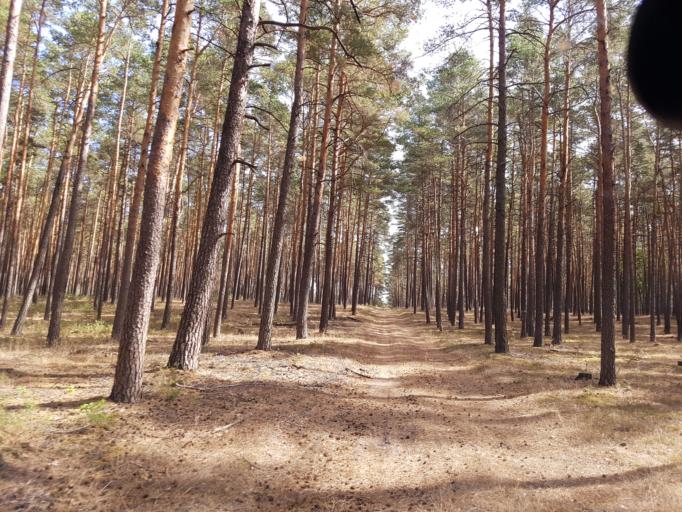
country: DE
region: Brandenburg
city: Sonnewalde
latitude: 51.7554
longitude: 13.6622
